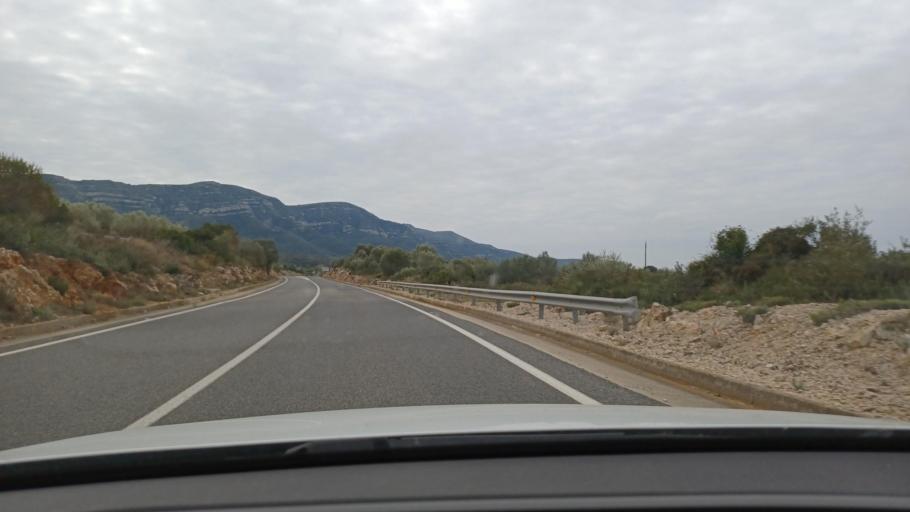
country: ES
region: Catalonia
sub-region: Provincia de Tarragona
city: Masdenverge
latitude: 40.6791
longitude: 0.5259
